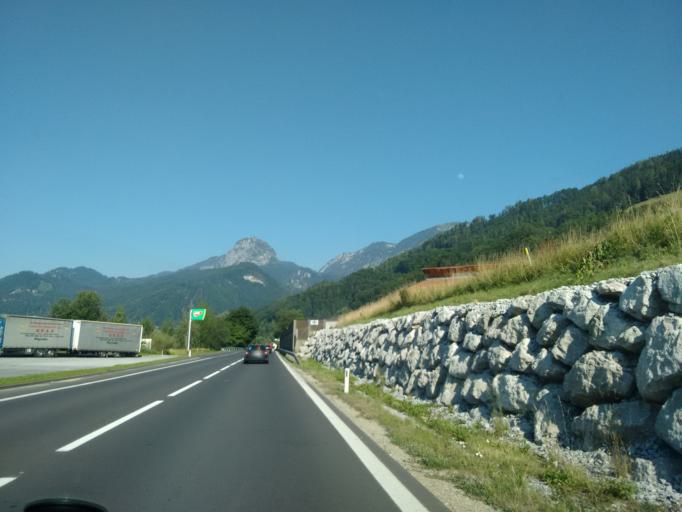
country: AT
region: Styria
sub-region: Politischer Bezirk Liezen
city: Liezen
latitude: 47.5684
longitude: 14.2286
